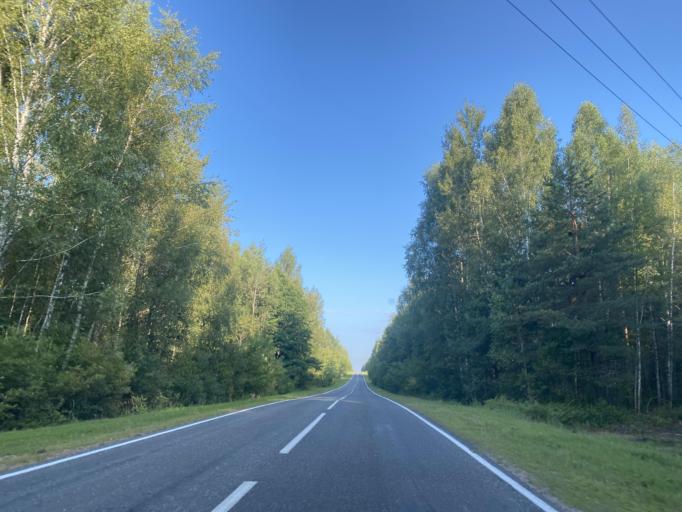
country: BY
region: Minsk
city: Loshnitsa
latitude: 54.1019
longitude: 28.6888
